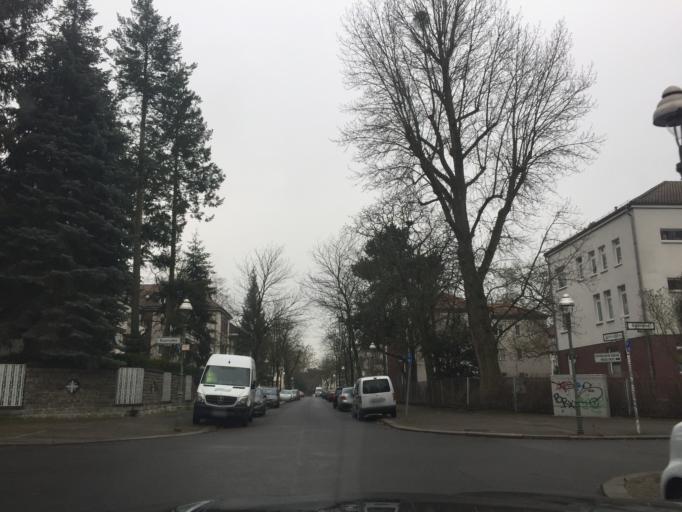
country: DE
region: Berlin
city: Westend
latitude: 52.5140
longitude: 13.2575
